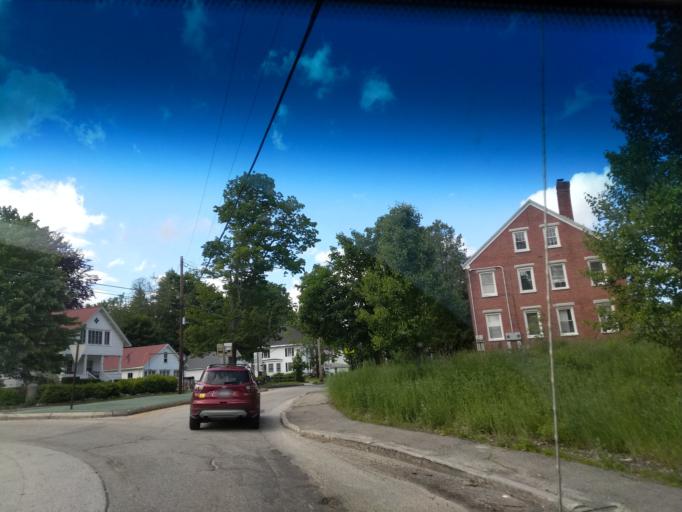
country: US
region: Maine
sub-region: Cumberland County
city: South Windham
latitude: 43.7284
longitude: -70.4251
